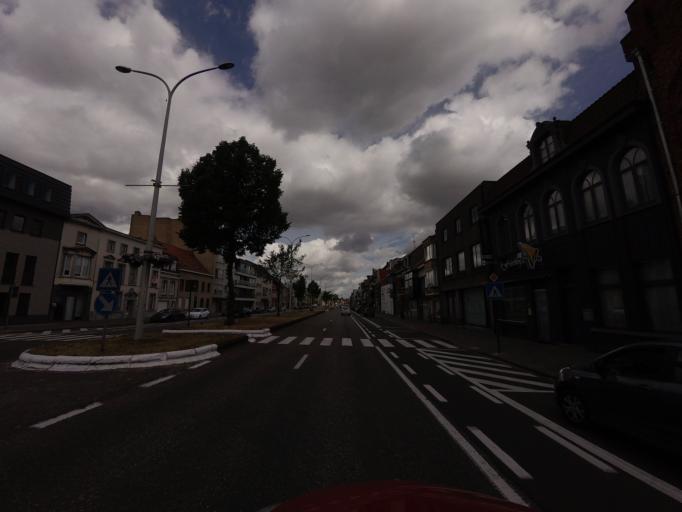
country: BE
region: Flanders
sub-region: Provincie Oost-Vlaanderen
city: Eeklo
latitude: 51.1866
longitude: 3.5620
